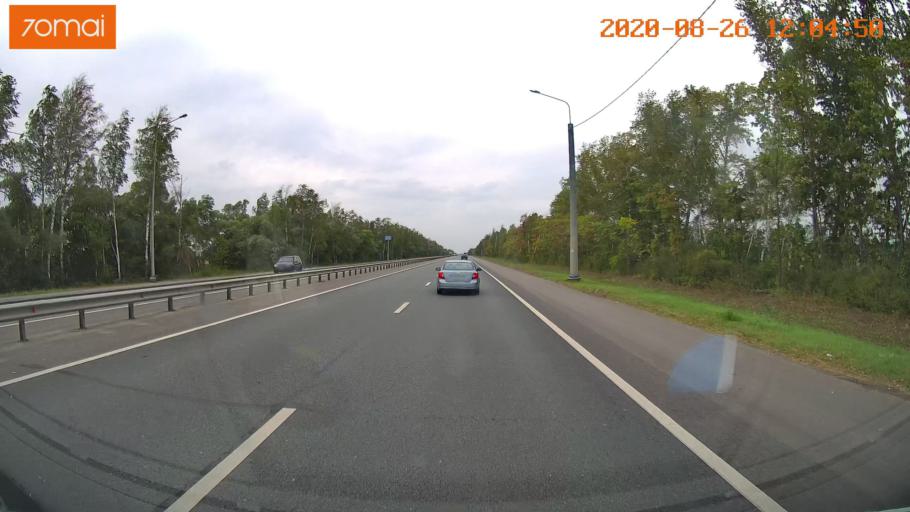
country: RU
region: Rjazan
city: Kiritsy
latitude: 54.3147
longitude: 40.1797
